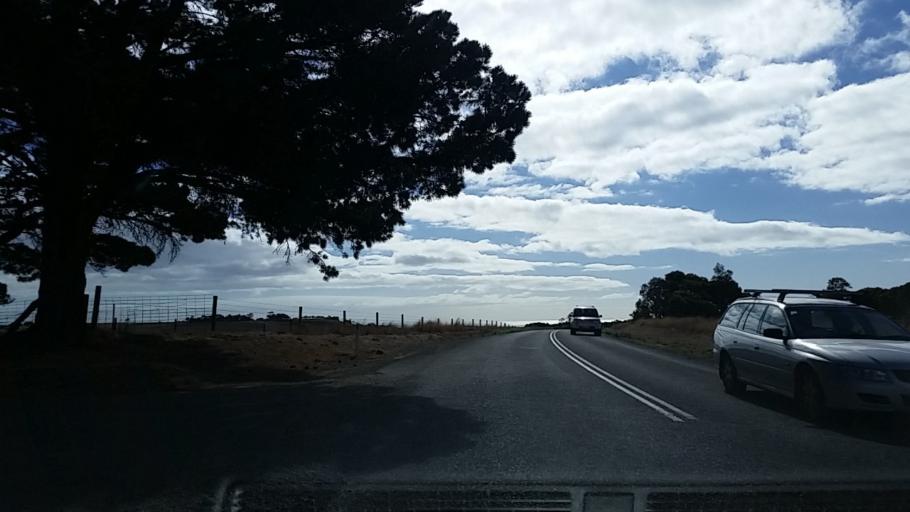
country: AU
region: South Australia
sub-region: Yankalilla
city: Normanville
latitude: -35.4157
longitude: 138.3755
